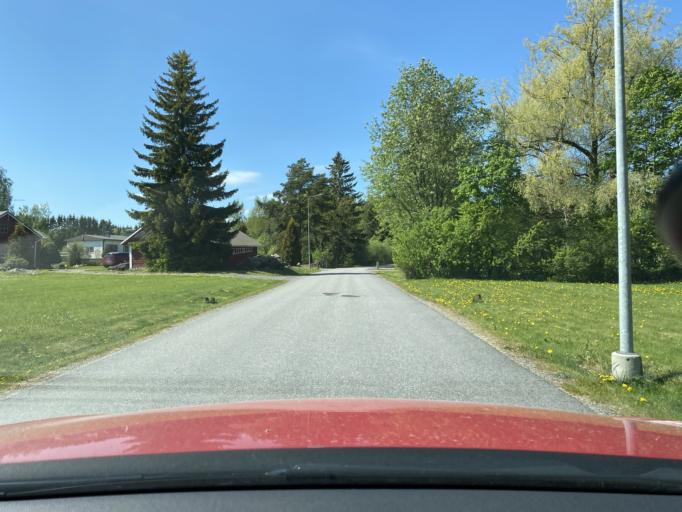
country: FI
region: Satakunta
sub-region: Rauma
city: Eura
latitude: 61.1108
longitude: 22.1408
